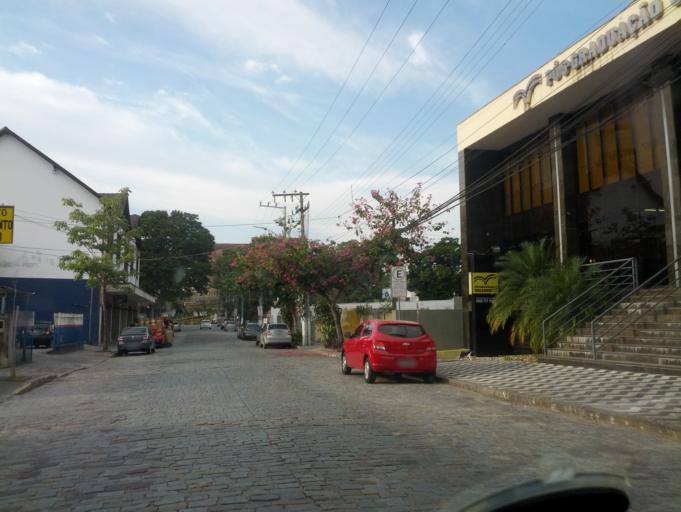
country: BR
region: Santa Catarina
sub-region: Blumenau
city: Blumenau
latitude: -26.9168
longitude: -49.0694
